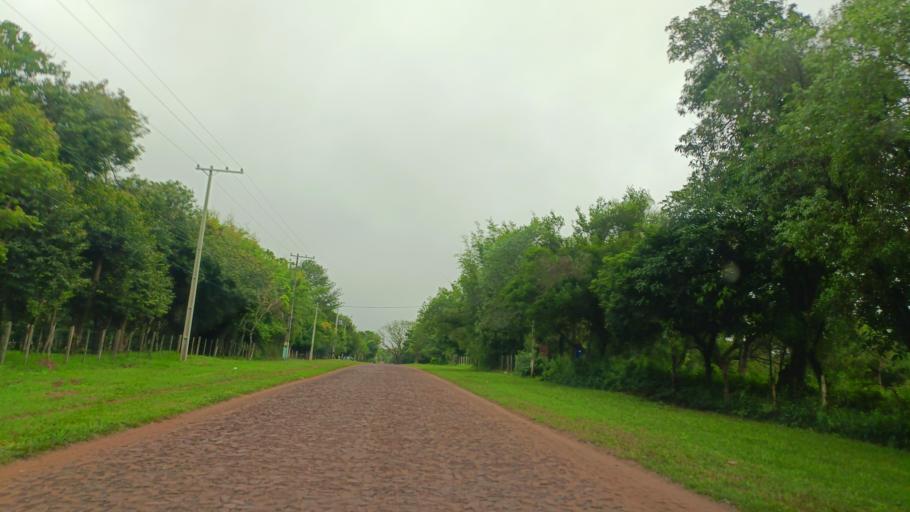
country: PY
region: Misiones
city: Santa Maria
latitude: -26.8617
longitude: -57.0254
